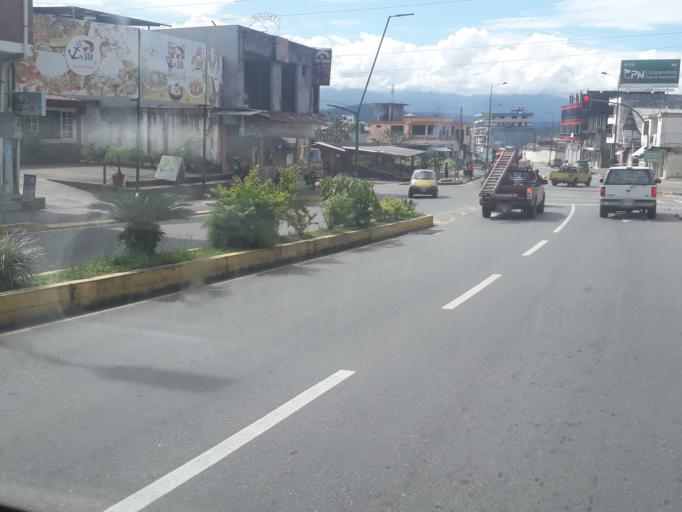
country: EC
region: Napo
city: Tena
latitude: -1.0075
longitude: -77.8094
